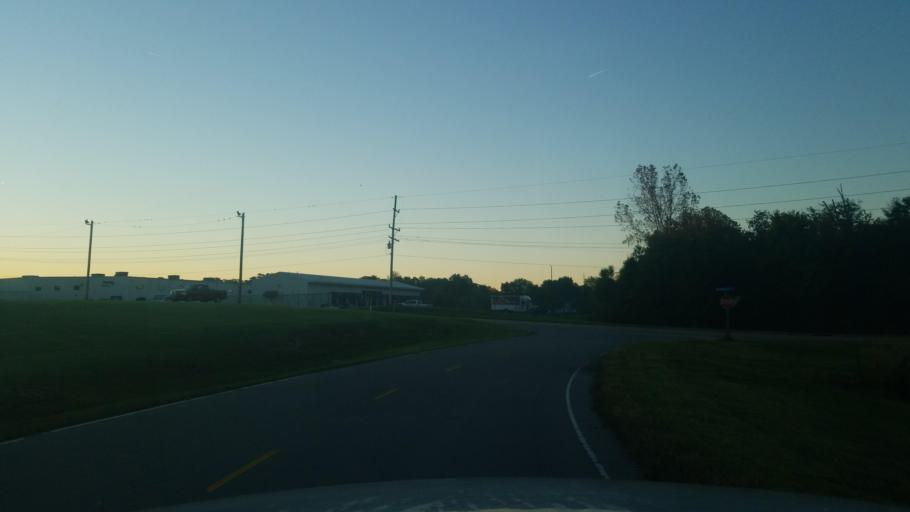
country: US
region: Illinois
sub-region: Williamson County
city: Energy
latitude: 37.7419
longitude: -89.0208
